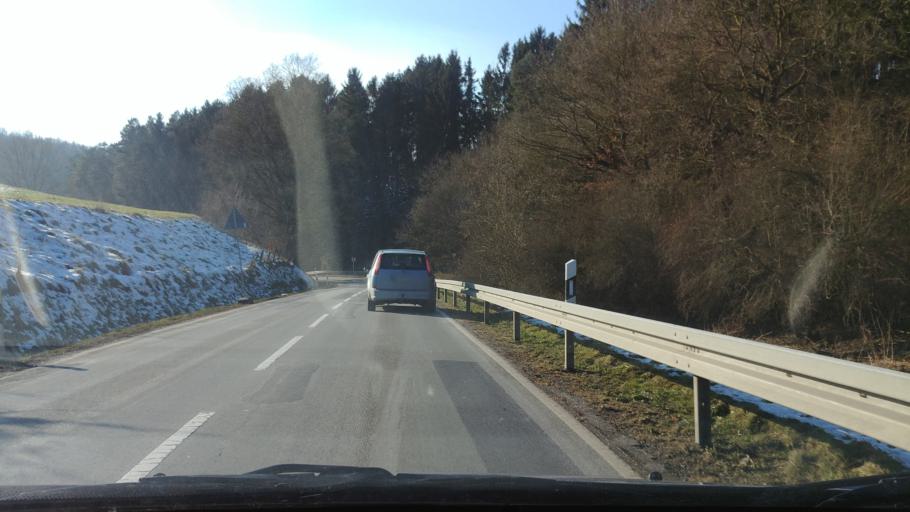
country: DE
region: Hesse
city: Trendelburg
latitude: 51.5743
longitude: 9.4471
